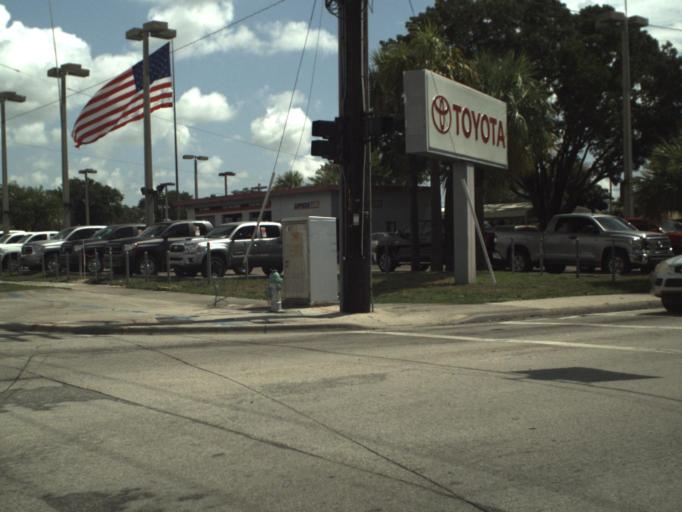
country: US
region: Florida
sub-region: Broward County
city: Pembroke Pines
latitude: 26.0249
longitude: -80.2081
